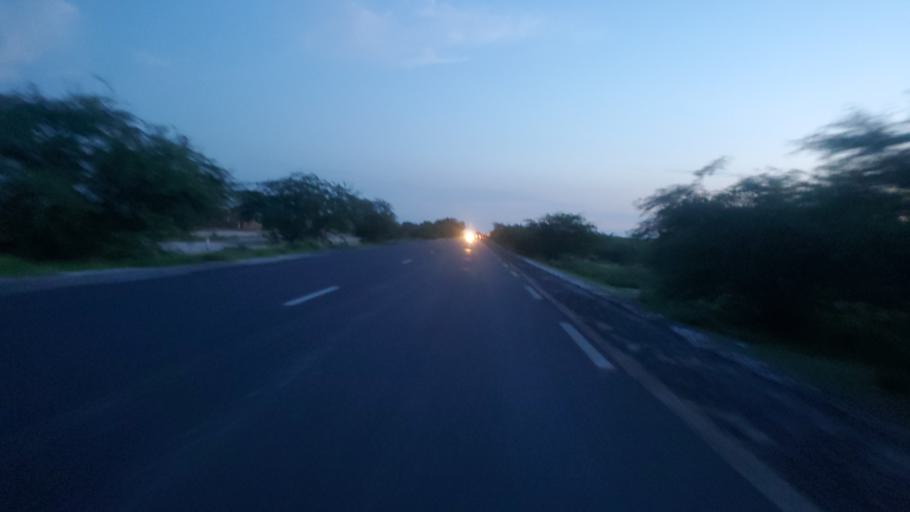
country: SN
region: Saint-Louis
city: Saint-Louis
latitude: 16.0617
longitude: -16.3956
